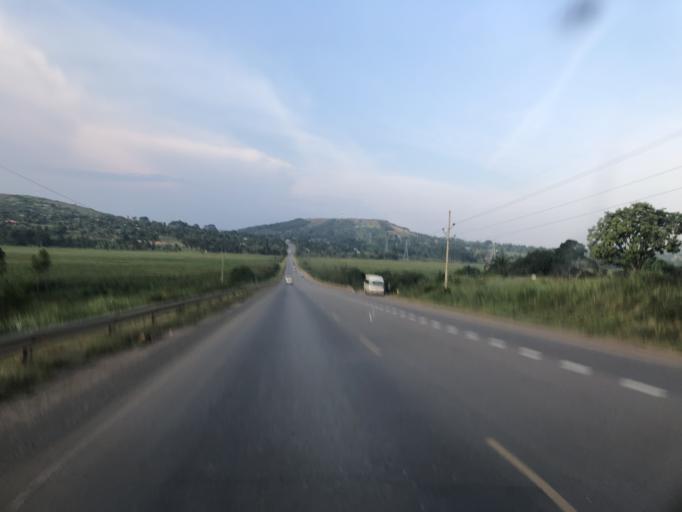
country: UG
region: Central Region
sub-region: Mpigi District
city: Mpigi
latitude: 0.1816
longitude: 32.2825
